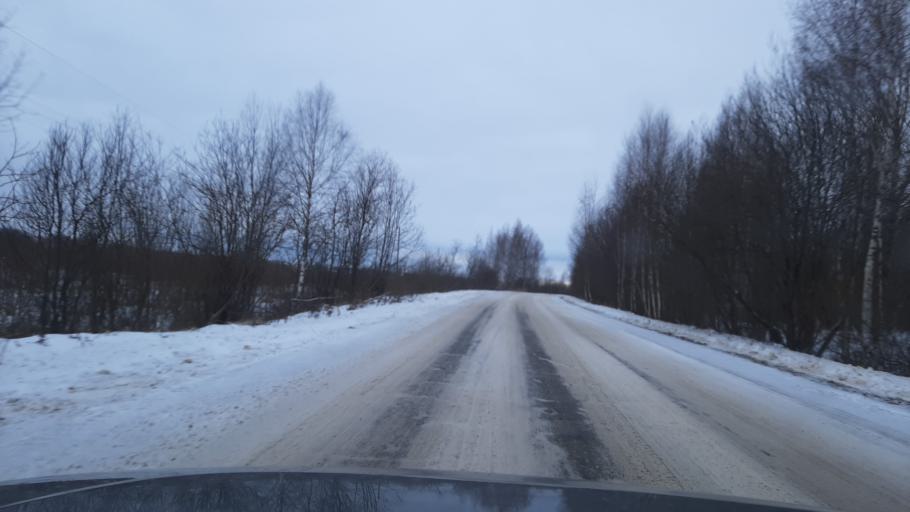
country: RU
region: Kostroma
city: Volgorechensk
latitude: 57.4400
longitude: 41.1104
